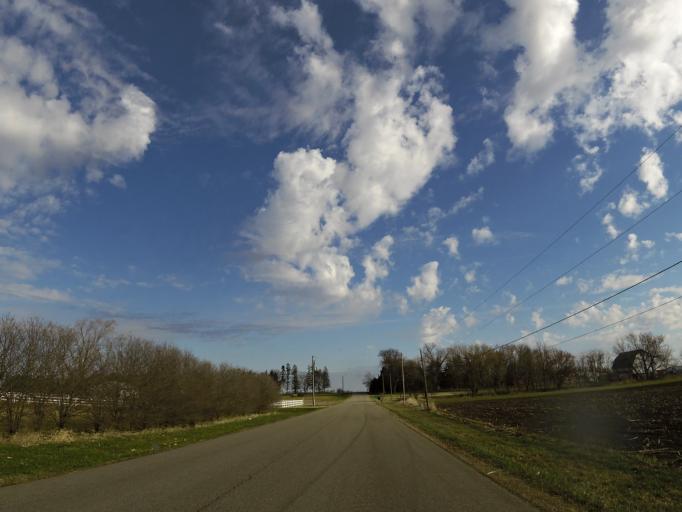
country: US
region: Minnesota
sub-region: Dakota County
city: Hastings
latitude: 44.7962
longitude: -92.8424
